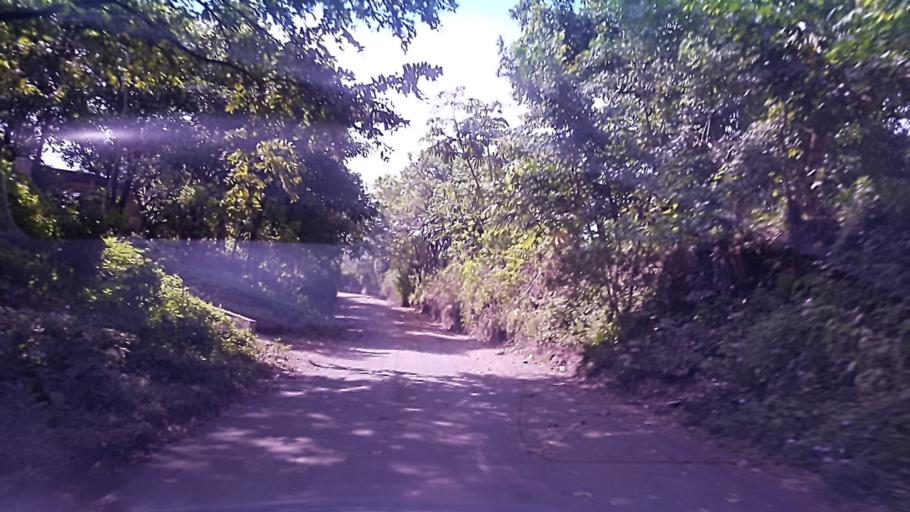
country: NI
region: Masaya
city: Ticuantepe
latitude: 11.9975
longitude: -86.2236
